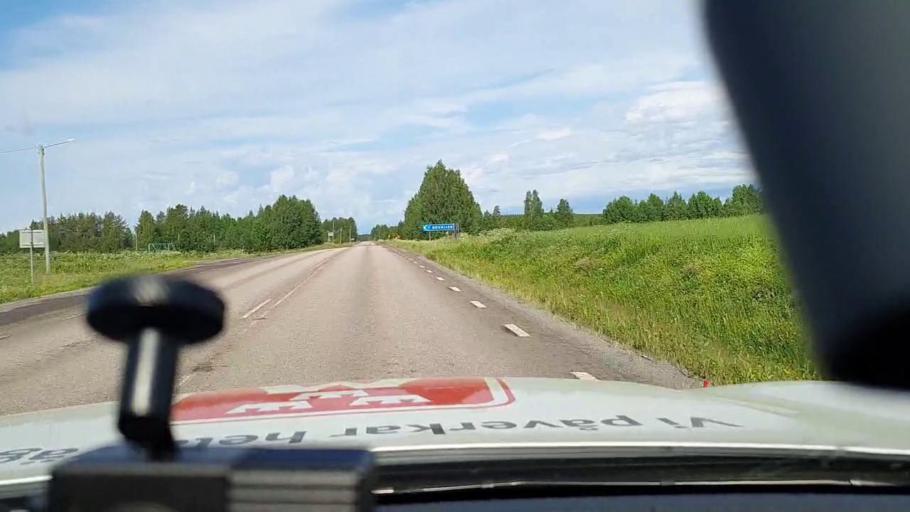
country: SE
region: Norrbotten
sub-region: Alvsbyns Kommun
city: AElvsbyn
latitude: 66.0150
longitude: 21.1621
